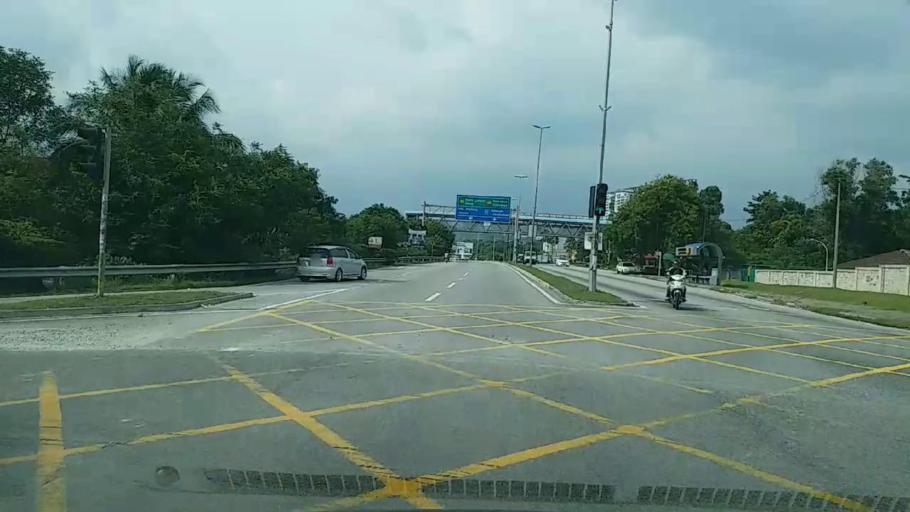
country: MY
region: Selangor
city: Subang Jaya
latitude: 2.9802
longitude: 101.6145
